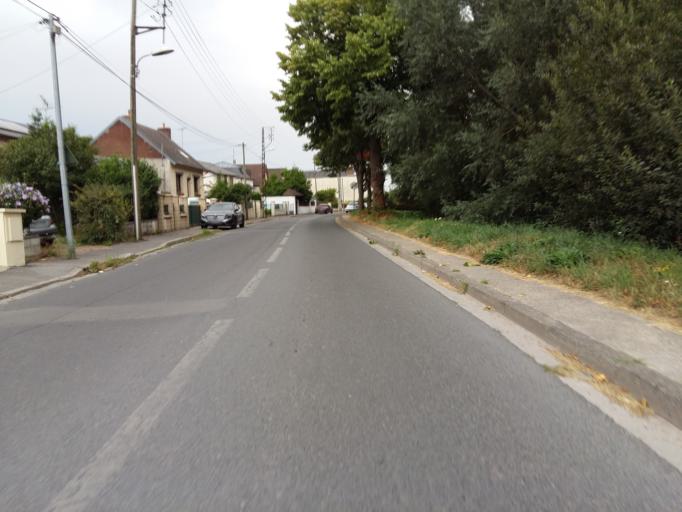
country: FR
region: Picardie
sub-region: Departement de la Somme
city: Rivery
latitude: 49.8901
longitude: 2.3271
